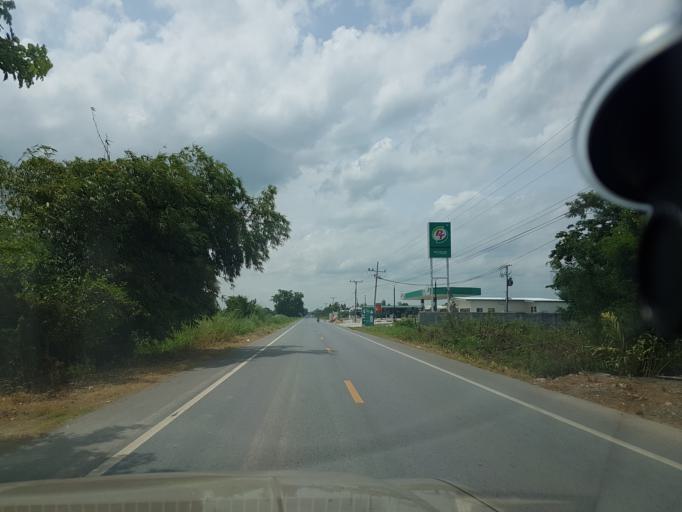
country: TH
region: Sara Buri
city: Nong Khae
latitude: 14.2677
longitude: 100.8919
